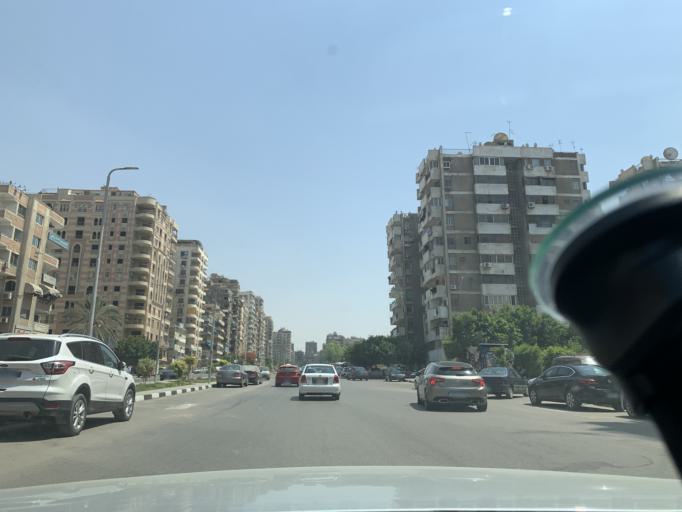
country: EG
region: Muhafazat al Qahirah
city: Cairo
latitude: 30.0665
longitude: 31.3489
